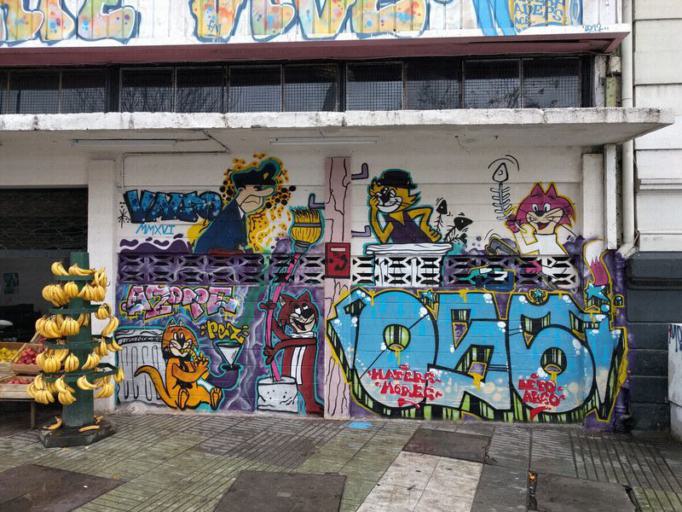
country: CL
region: Valparaiso
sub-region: Provincia de Valparaiso
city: Valparaiso
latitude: -33.0443
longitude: -71.6226
